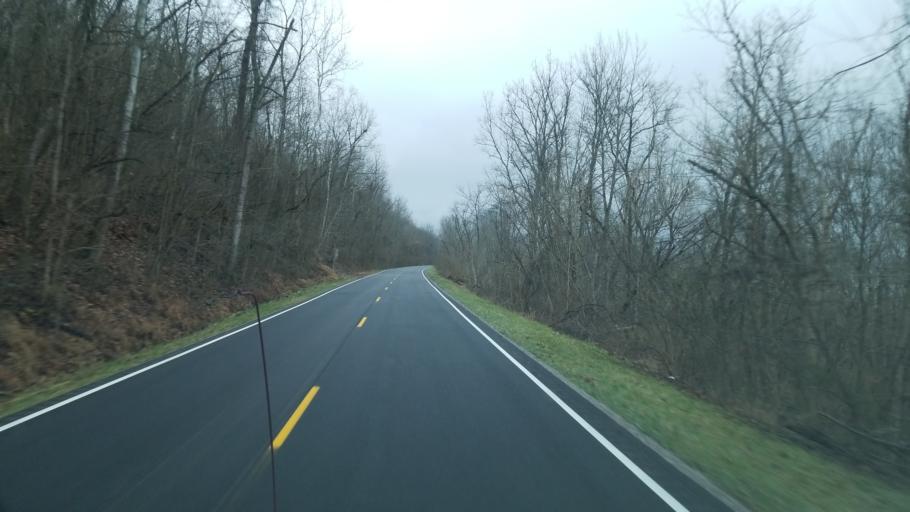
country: US
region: Ohio
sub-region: Brown County
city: Ripley
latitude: 38.7612
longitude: -83.9162
